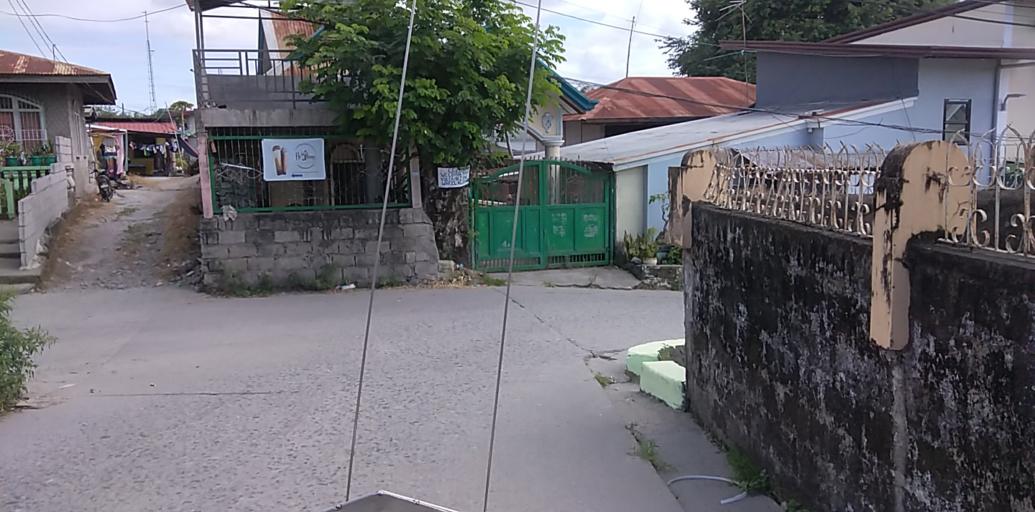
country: PH
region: Central Luzon
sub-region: Province of Pampanga
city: Porac
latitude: 15.0766
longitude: 120.5345
